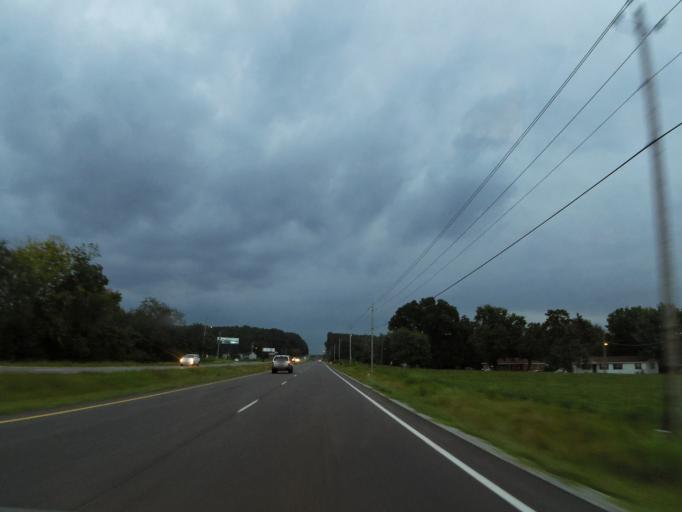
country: US
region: Alabama
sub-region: Madison County
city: Moores Mill
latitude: 34.7664
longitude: -86.4891
